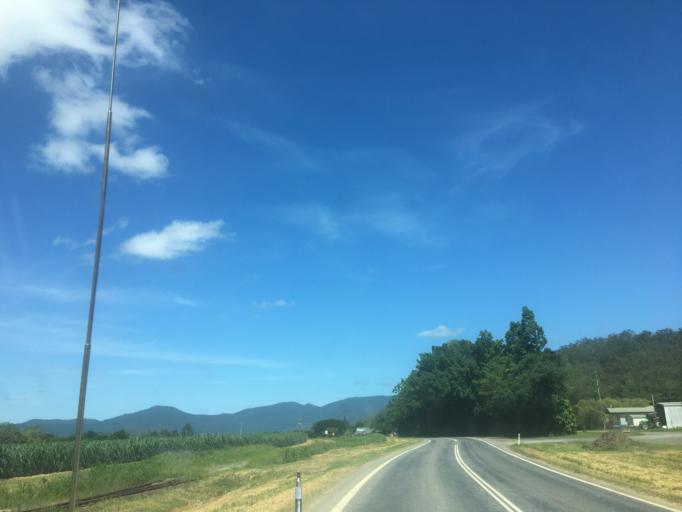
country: AU
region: Queensland
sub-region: Cairns
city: Woree
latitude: -17.0673
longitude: 145.7494
